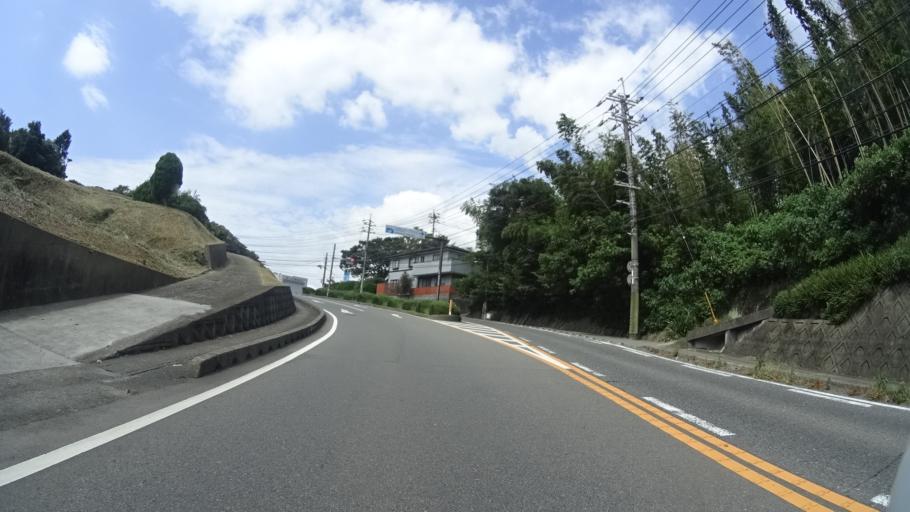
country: JP
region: Yamaguchi
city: Shimonoseki
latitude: 33.9721
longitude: 130.9526
